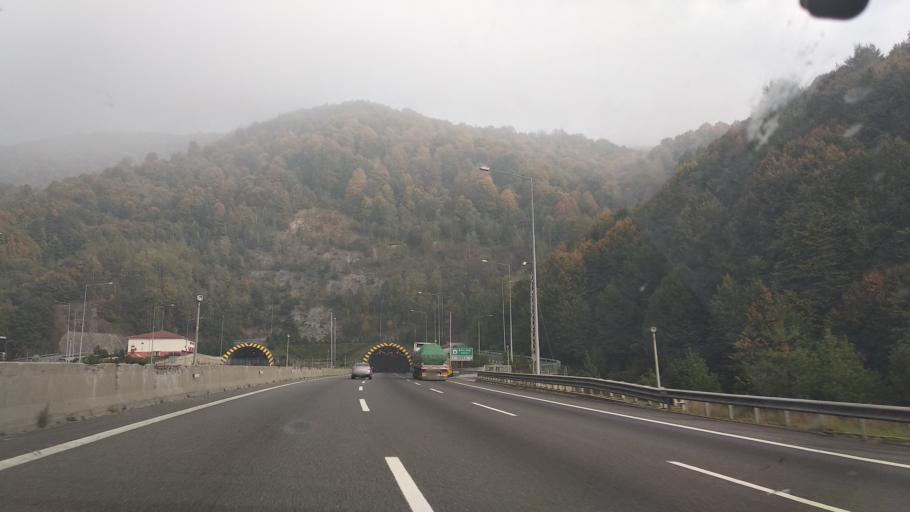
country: TR
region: Duzce
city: Kaynasli
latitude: 40.7583
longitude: 31.4476
